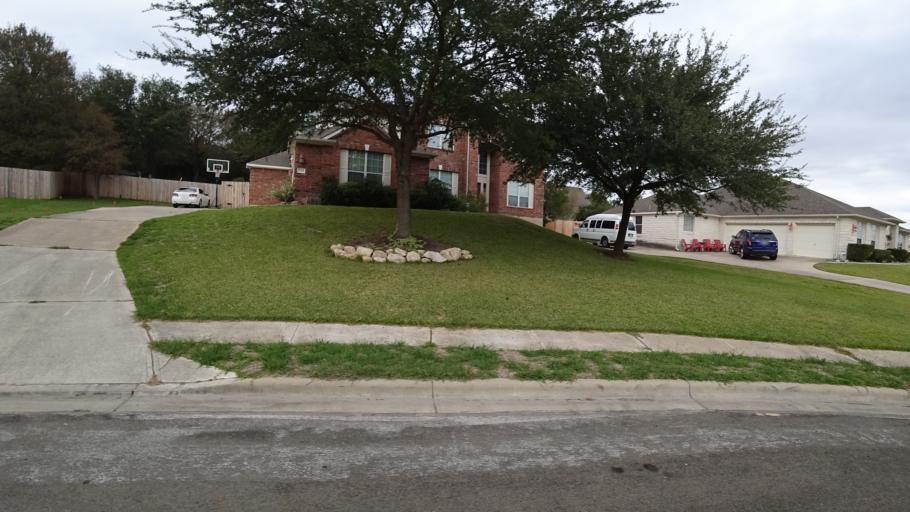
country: US
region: Texas
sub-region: Travis County
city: Shady Hollow
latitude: 30.1480
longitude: -97.8587
